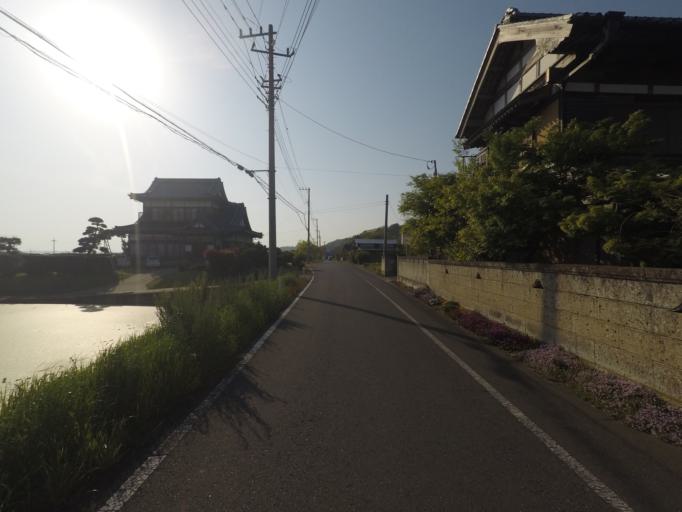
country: JP
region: Ibaraki
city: Ami
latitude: 36.0672
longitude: 140.2848
